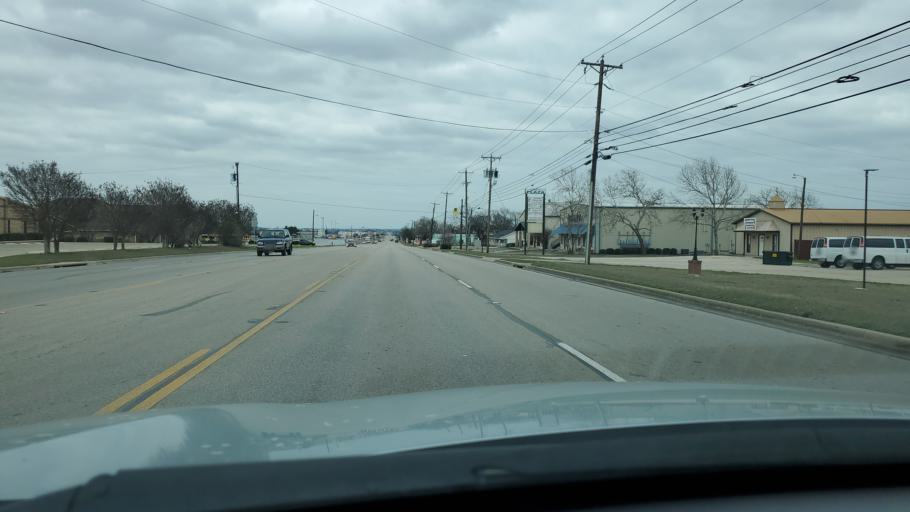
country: US
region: Texas
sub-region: Bell County
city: Killeen
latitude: 31.0831
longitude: -97.7442
